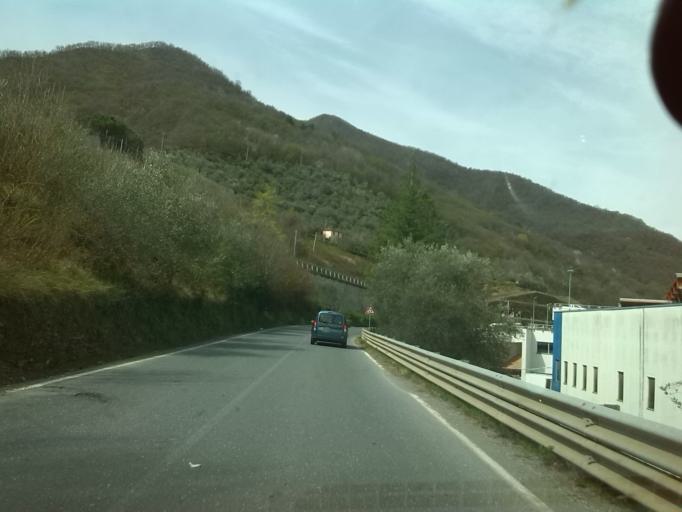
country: IT
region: Liguria
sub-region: Provincia di Imperia
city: Pieve di Teco
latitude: 44.0376
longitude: 7.9272
